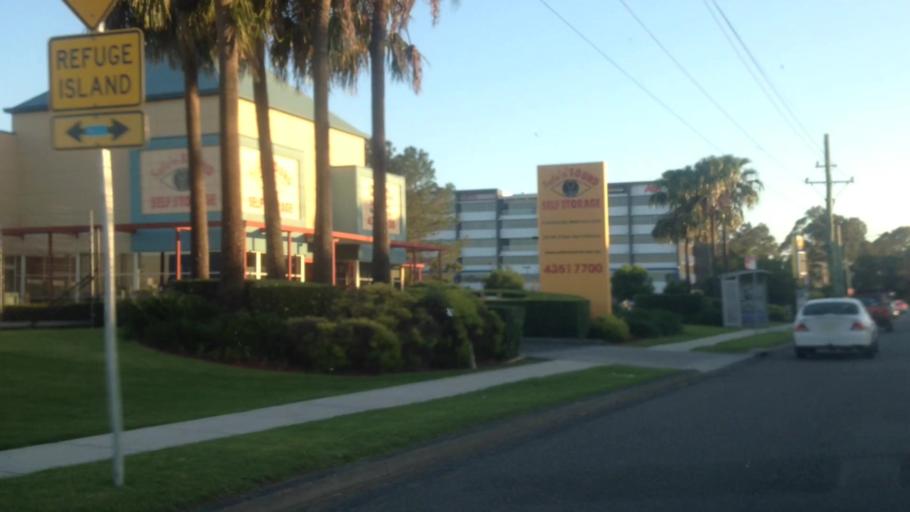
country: AU
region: New South Wales
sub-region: Wyong Shire
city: Chittaway Bay
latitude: -33.3113
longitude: 151.4224
